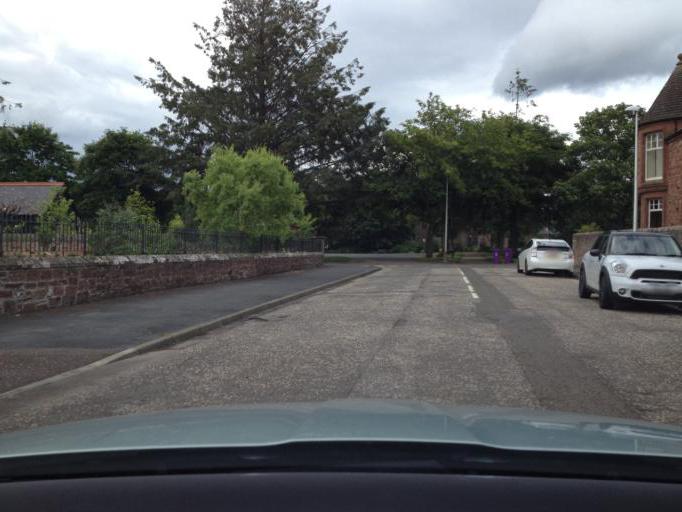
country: GB
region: Scotland
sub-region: Angus
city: Brechin
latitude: 56.8113
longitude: -2.6586
